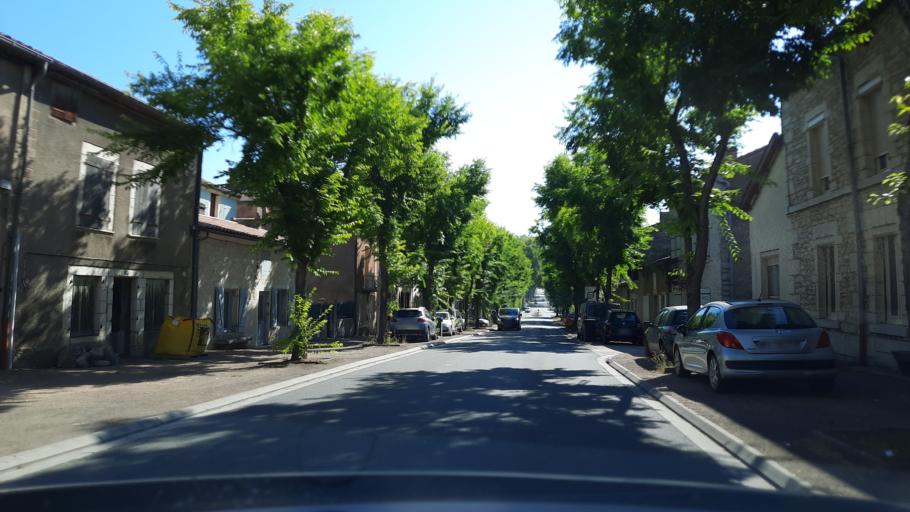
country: FR
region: Midi-Pyrenees
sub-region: Departement du Tarn-et-Garonne
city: Septfonds
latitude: 44.1772
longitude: 1.6205
